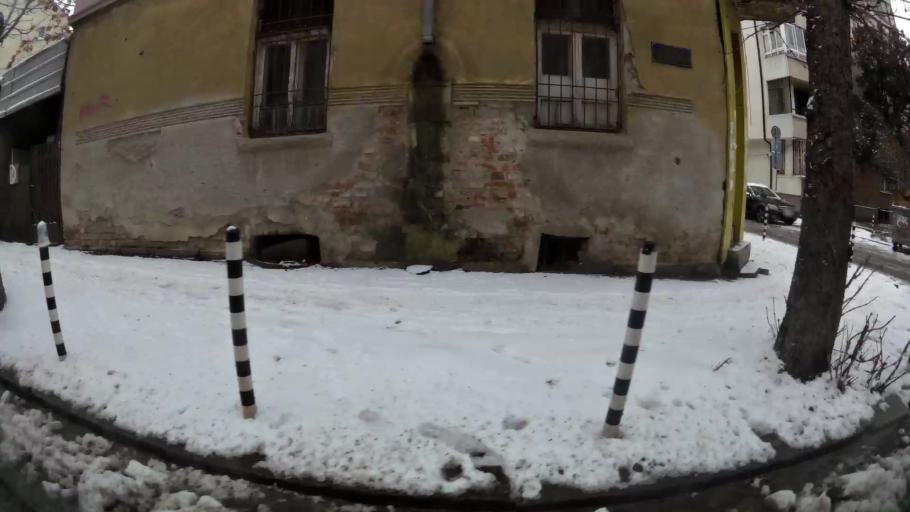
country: BG
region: Sofia-Capital
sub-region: Stolichna Obshtina
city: Sofia
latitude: 42.7067
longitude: 23.3266
